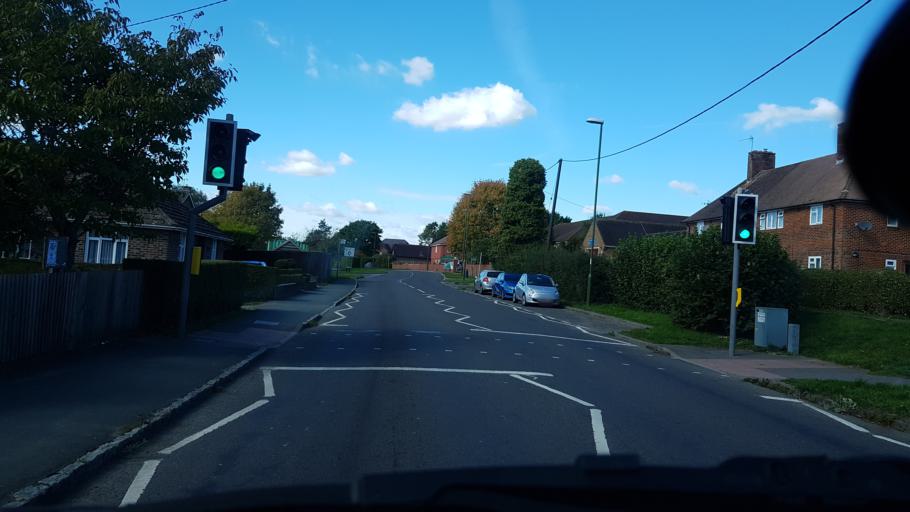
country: GB
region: England
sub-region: West Sussex
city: Billingshurst
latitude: 51.0216
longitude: -0.4556
